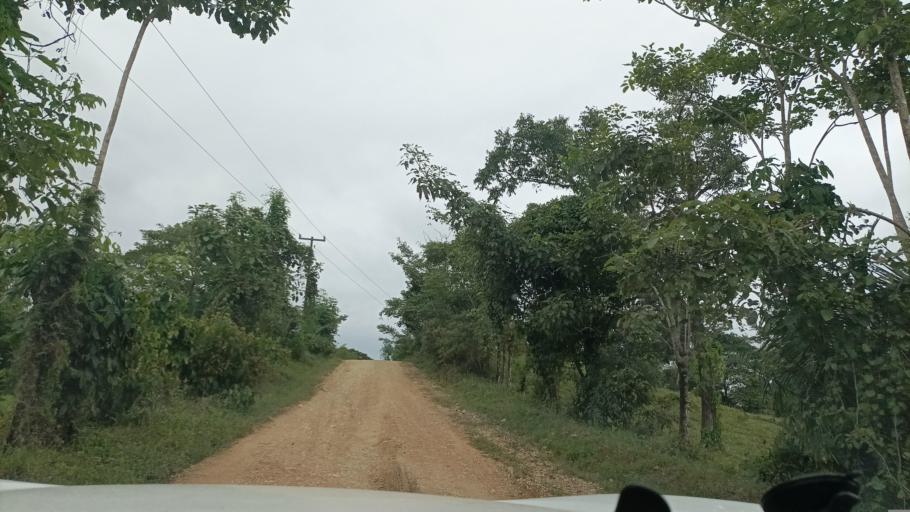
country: MX
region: Veracruz
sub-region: Uxpanapa
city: Poblado Cinco
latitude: 17.4887
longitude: -94.5724
